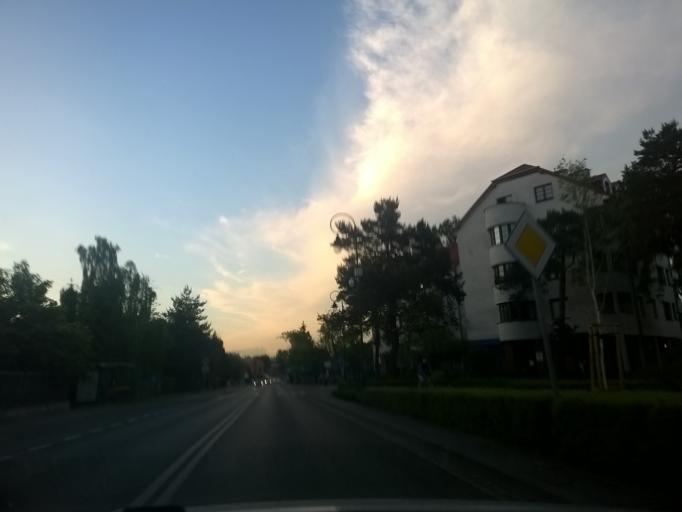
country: PL
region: Masovian Voivodeship
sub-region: Powiat piaseczynski
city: Konstancin-Jeziorna
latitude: 52.0886
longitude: 21.1215
